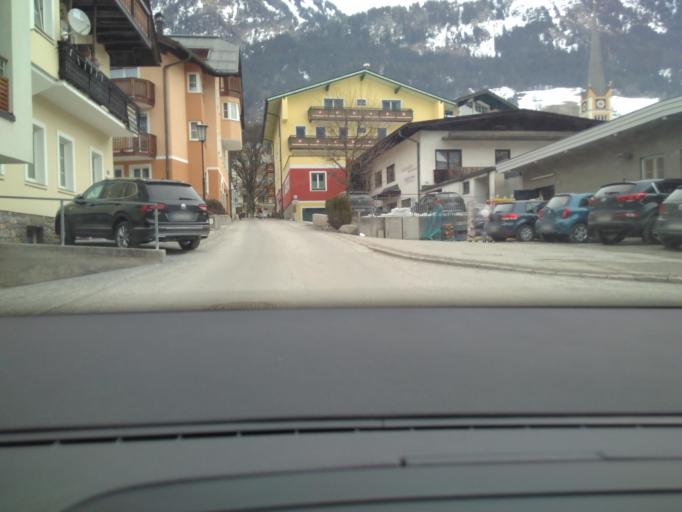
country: AT
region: Salzburg
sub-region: Politischer Bezirk Sankt Johann im Pongau
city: Bad Hofgastein
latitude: 47.1715
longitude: 13.1044
